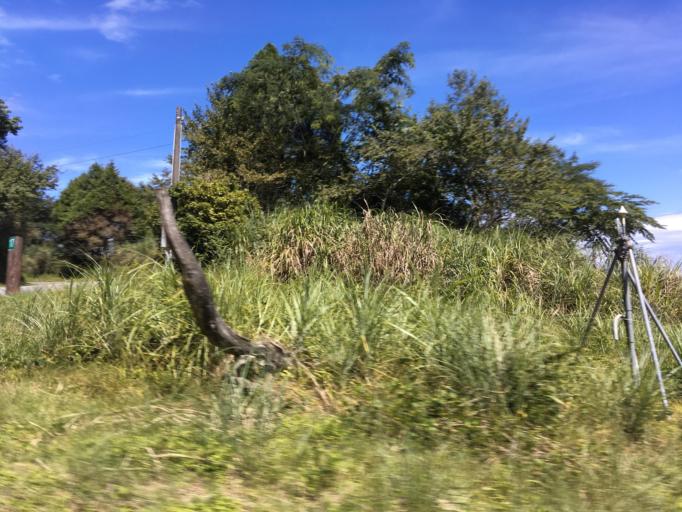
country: TW
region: Taiwan
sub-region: Yilan
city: Yilan
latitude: 24.5254
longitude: 121.5195
